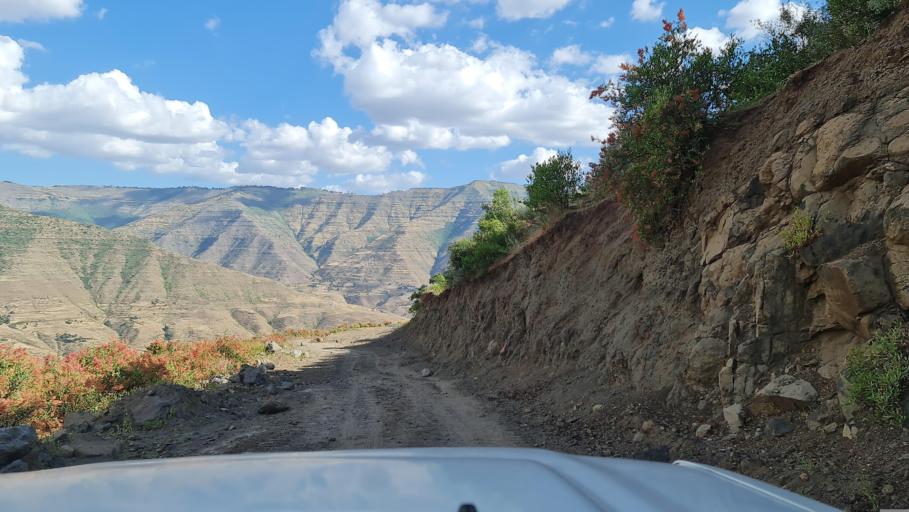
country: ET
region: Amhara
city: Debark'
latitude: 13.1241
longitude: 38.0194
